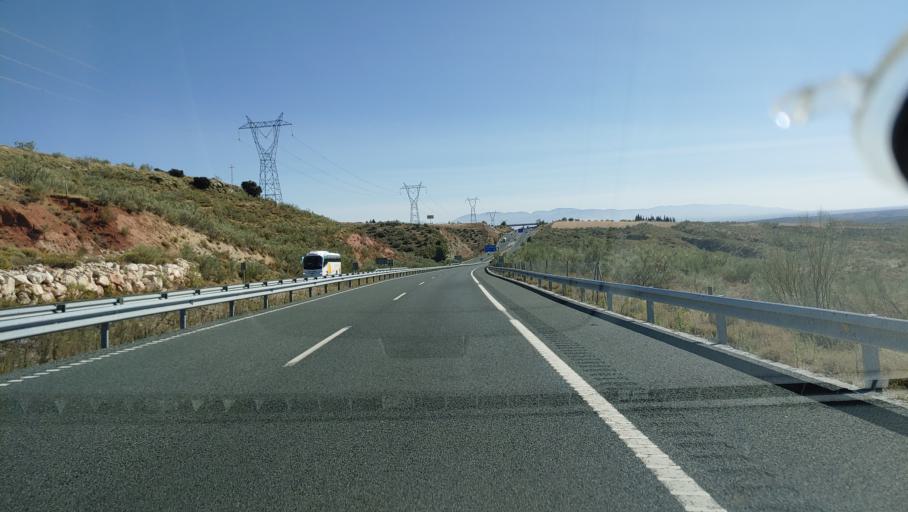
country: ES
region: Andalusia
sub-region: Provincia de Granada
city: Diezma
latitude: 37.3148
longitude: -3.3475
